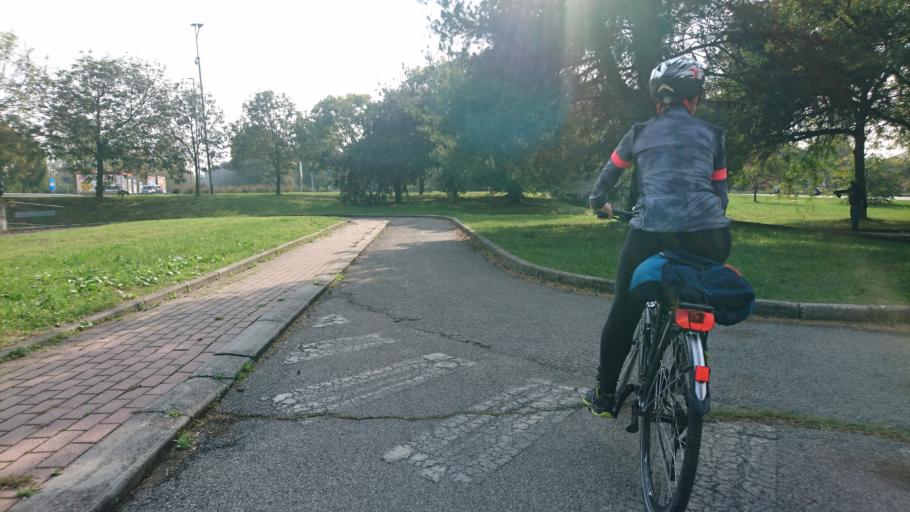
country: IT
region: Veneto
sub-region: Provincia di Rovigo
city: Rovigo
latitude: 45.0727
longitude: 11.7823
